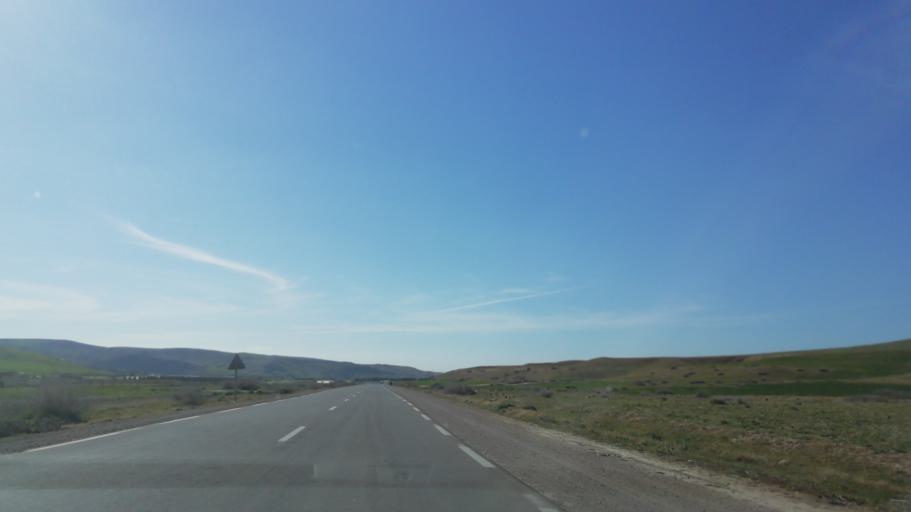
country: DZ
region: Mascara
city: Oued el Abtal
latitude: 35.4497
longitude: 0.7978
